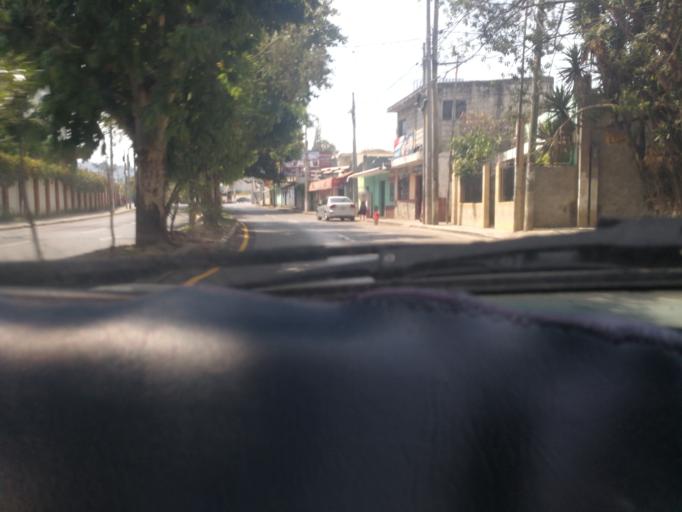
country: GT
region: Guatemala
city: Guatemala City
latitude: 14.6183
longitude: -90.4736
